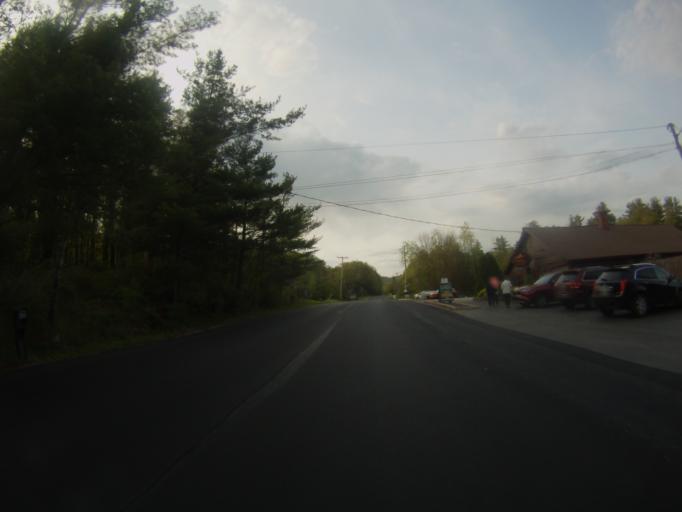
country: US
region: New York
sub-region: Essex County
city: Ticonderoga
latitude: 43.8043
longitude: -73.4880
